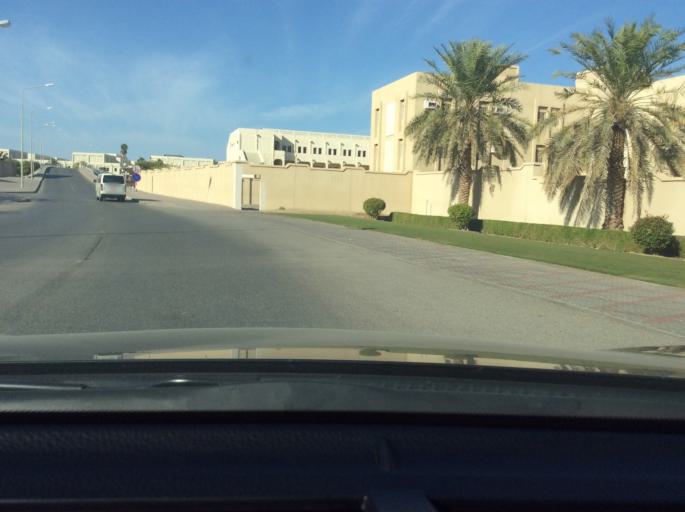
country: OM
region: Muhafazat Masqat
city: As Sib al Jadidah
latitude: 23.5847
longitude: 58.1713
